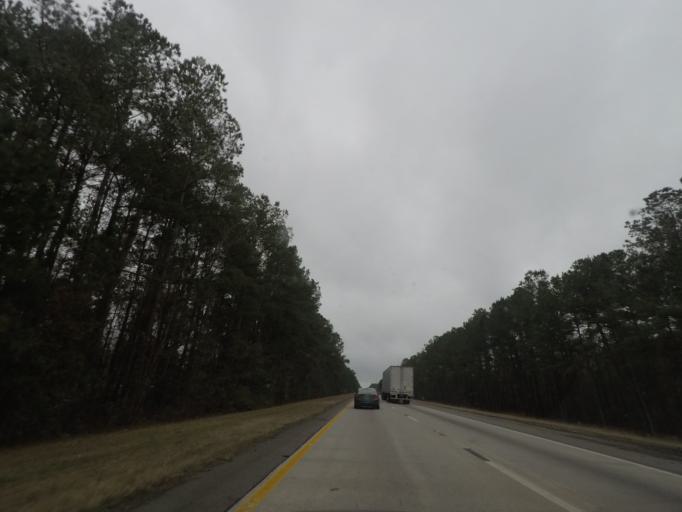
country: US
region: South Carolina
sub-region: Colleton County
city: Walterboro
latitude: 33.0144
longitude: -80.6670
